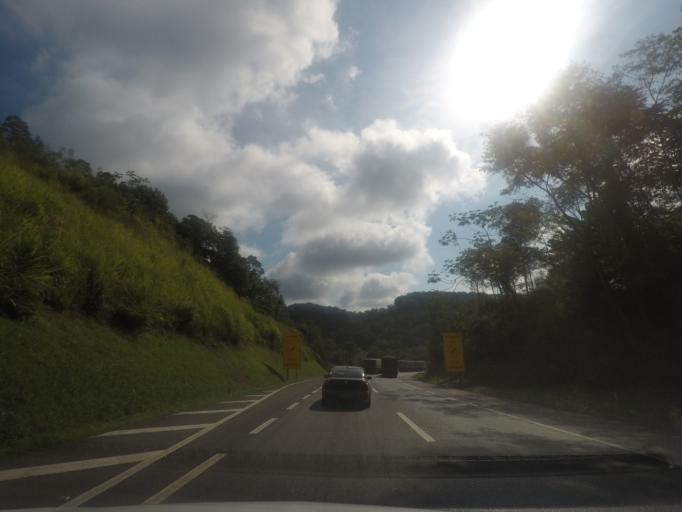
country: BR
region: Parana
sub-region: Antonina
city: Antonina
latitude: -25.5631
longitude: -48.8132
